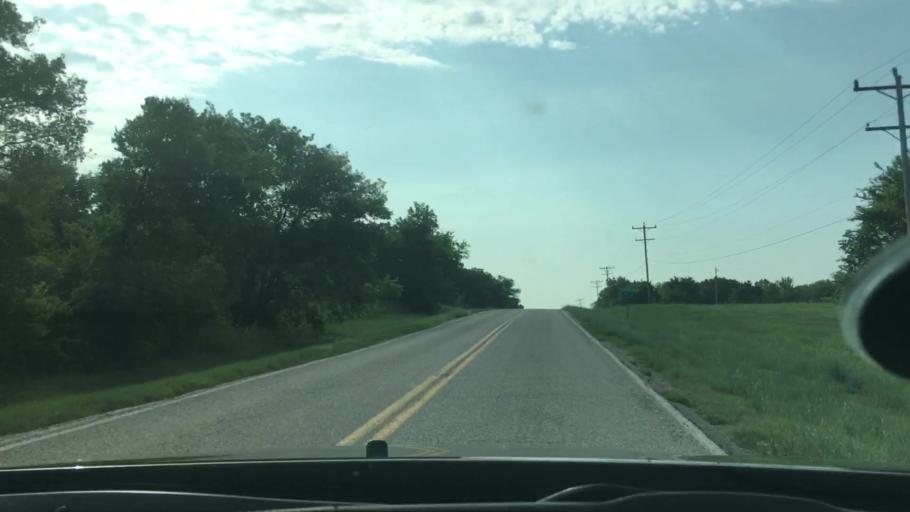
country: US
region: Oklahoma
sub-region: Johnston County
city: Tishomingo
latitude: 34.1497
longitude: -96.5547
